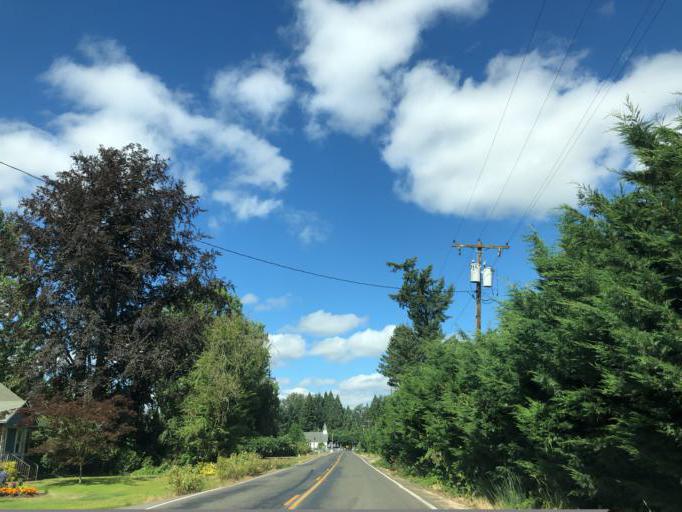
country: US
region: Oregon
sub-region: Marion County
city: Mount Angel
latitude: 45.1003
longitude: -122.7396
